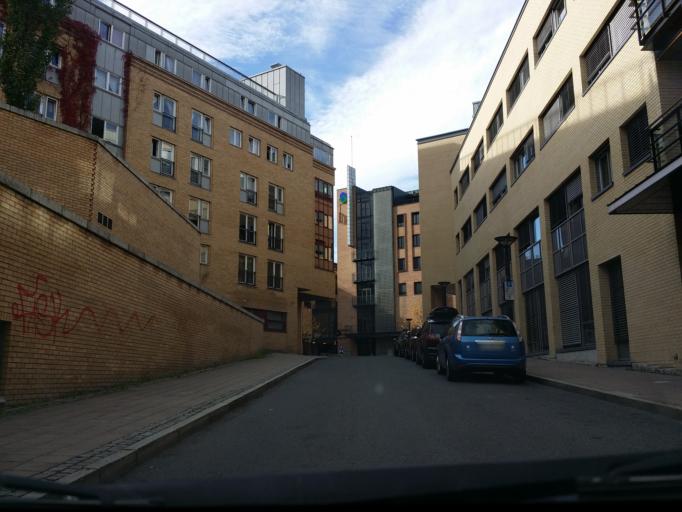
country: NO
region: Akershus
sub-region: Baerum
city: Sandvika
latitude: 59.8905
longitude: 10.5222
